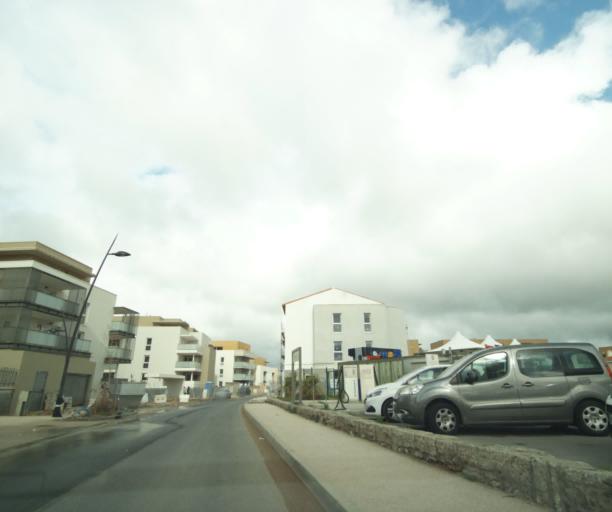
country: FR
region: Languedoc-Roussillon
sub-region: Departement de l'Herault
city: Pignan
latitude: 43.5858
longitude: 3.7714
